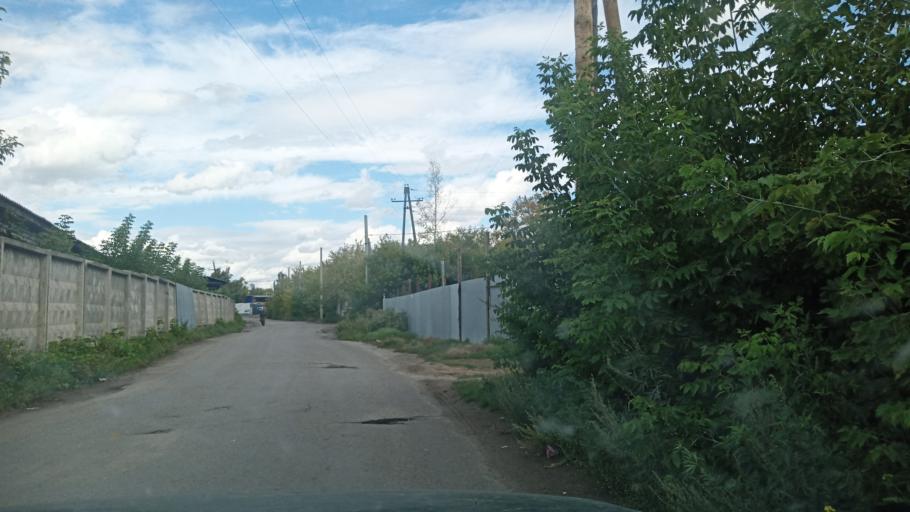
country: RU
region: Altai Krai
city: Zaton
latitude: 53.3328
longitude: 83.8066
